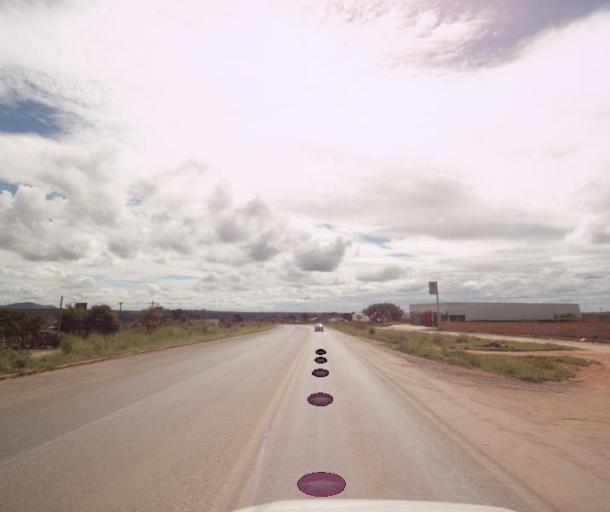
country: BR
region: Goias
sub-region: Uruacu
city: Uruacu
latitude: -14.5152
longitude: -49.1509
